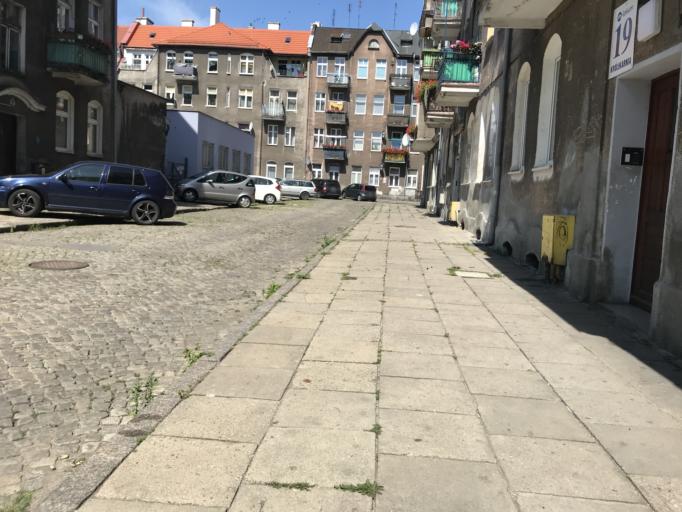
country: PL
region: Pomeranian Voivodeship
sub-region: Gdansk
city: Gdansk
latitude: 54.3421
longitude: 18.6643
